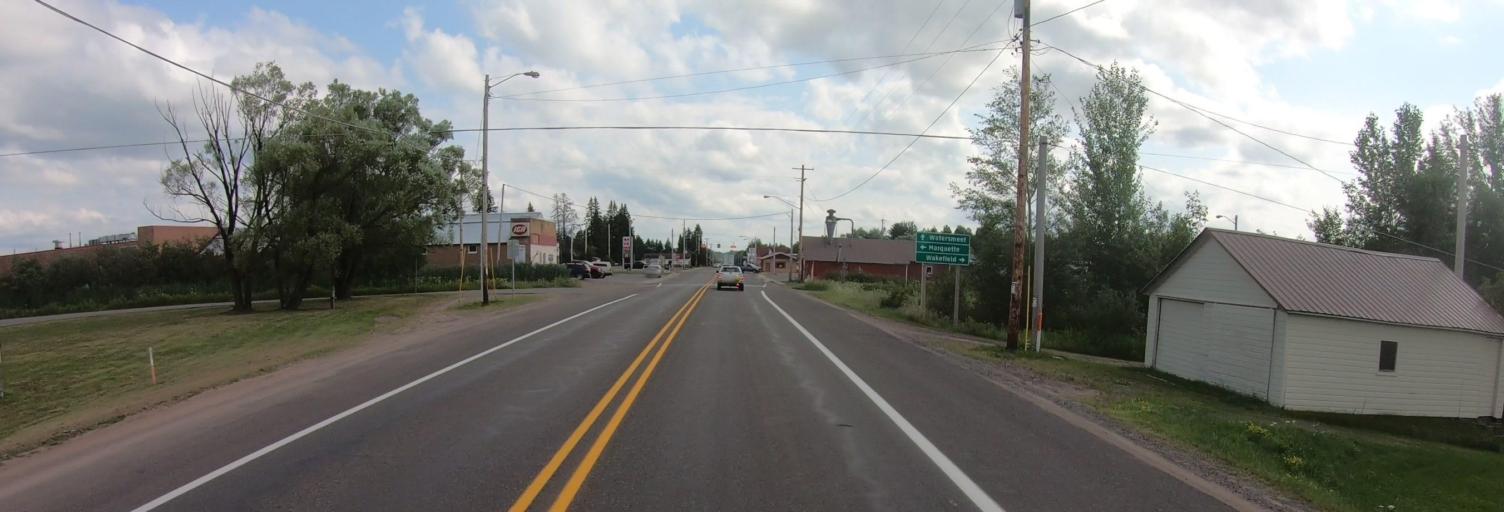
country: US
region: Michigan
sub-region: Ontonagon County
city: Ontonagon
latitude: 46.5364
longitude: -89.1786
